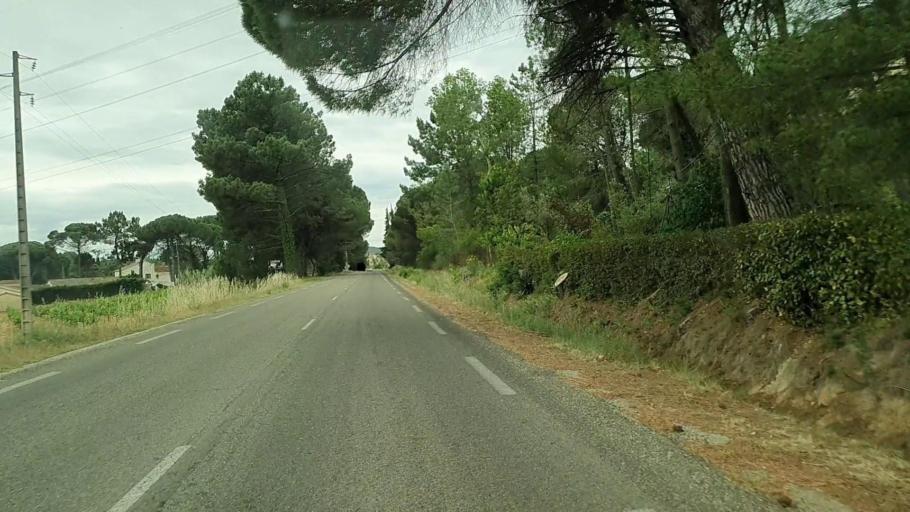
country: FR
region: Languedoc-Roussillon
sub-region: Departement du Gard
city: Tresques
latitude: 44.1201
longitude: 4.5967
